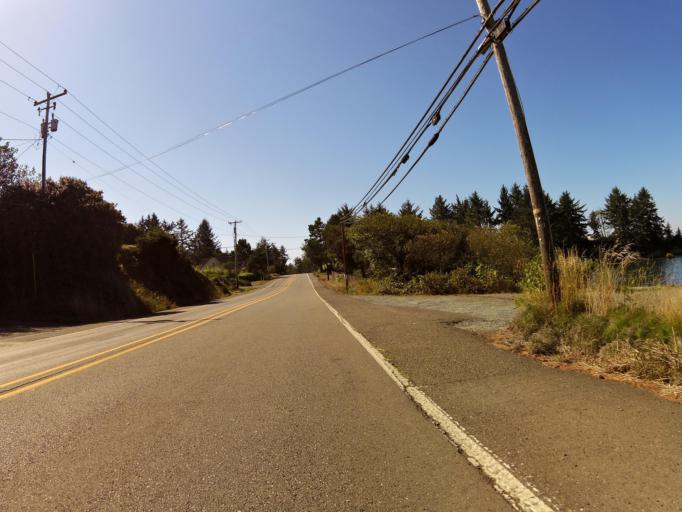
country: US
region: Oregon
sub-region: Coos County
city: Barview
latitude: 43.3585
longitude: -124.3083
